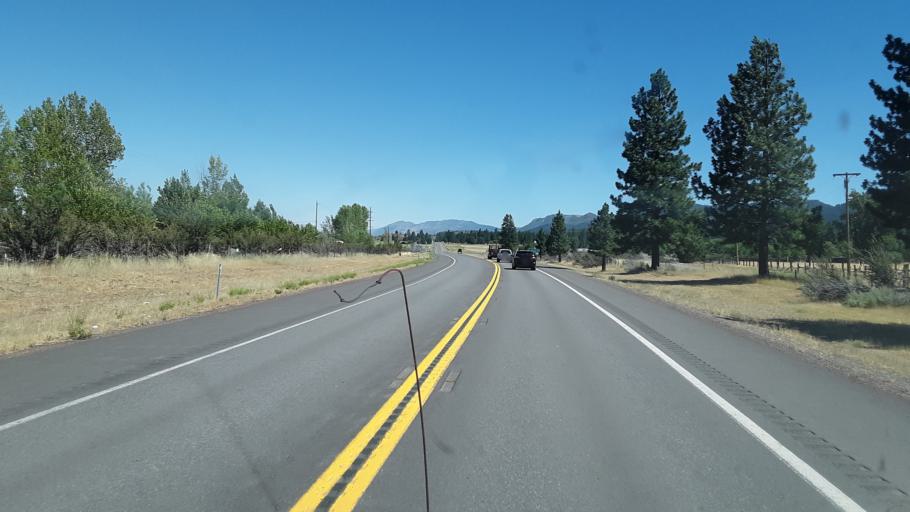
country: US
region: California
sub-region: Lassen County
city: Janesville
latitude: 40.3175
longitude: -120.5421
